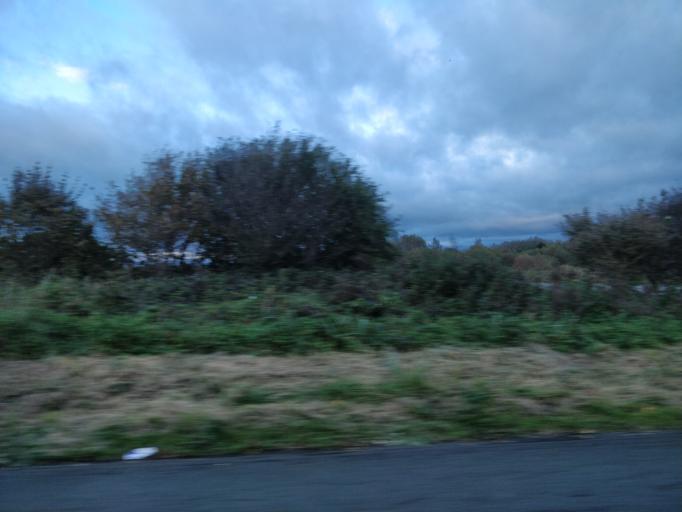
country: GB
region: England
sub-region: Sefton
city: Southport
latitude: 53.6655
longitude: -2.9908
